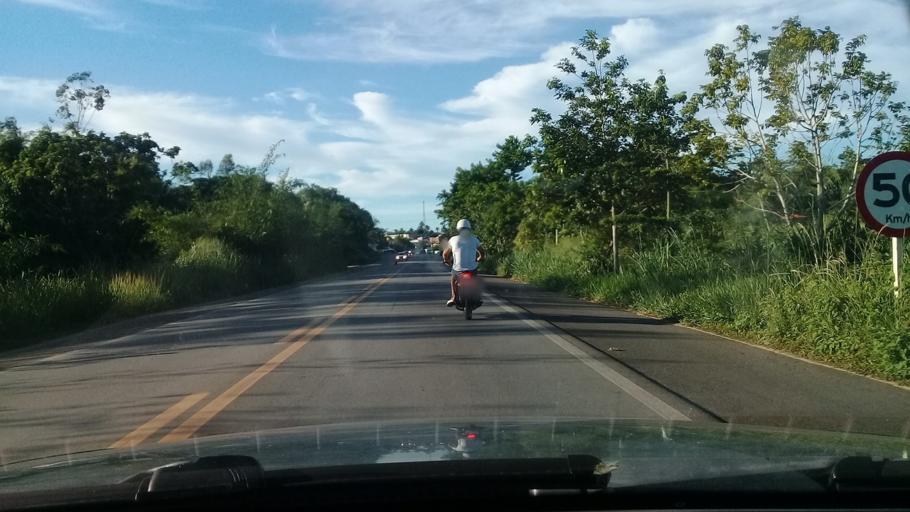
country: BR
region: Pernambuco
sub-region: Nazare Da Mata
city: Nazare da Mata
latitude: -7.7571
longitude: -35.2333
